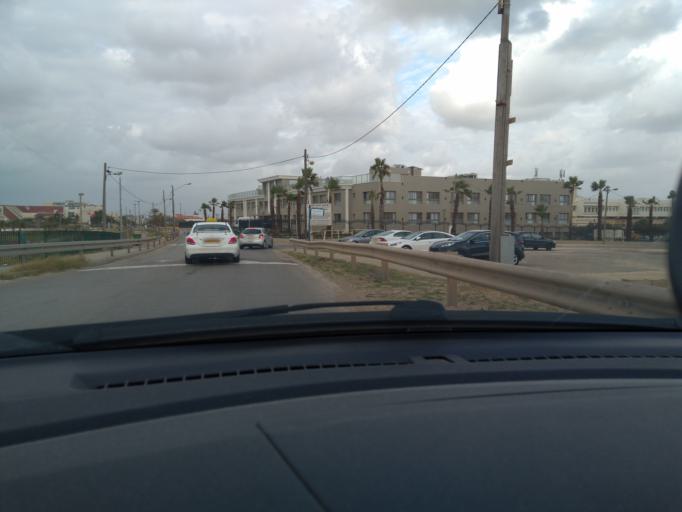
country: IL
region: Central District
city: Netanya
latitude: 32.3443
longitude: 34.8541
